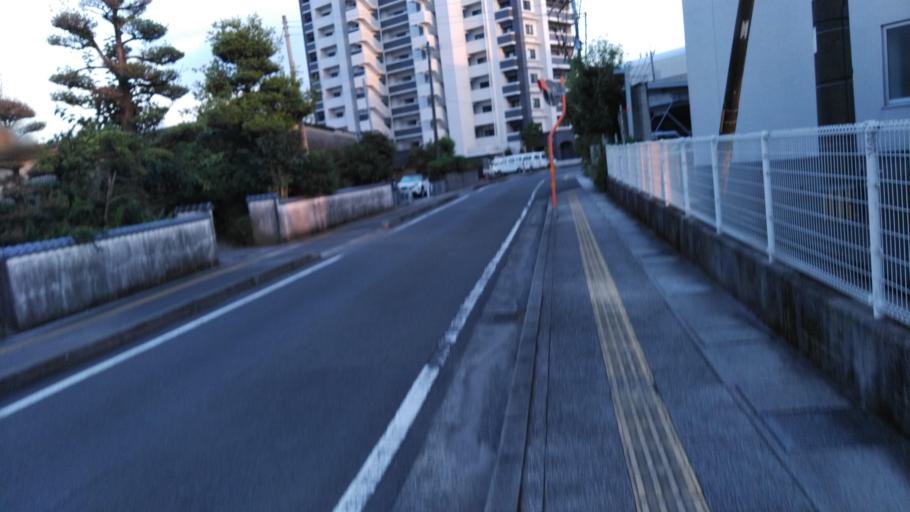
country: JP
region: Kagoshima
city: Kokubu-matsuki
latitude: 31.7420
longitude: 130.7634
